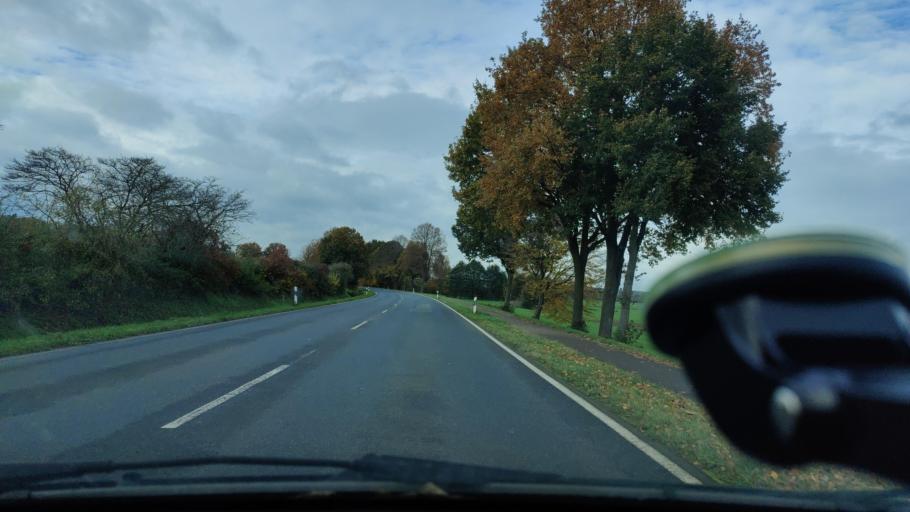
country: DE
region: North Rhine-Westphalia
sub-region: Regierungsbezirk Dusseldorf
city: Sonsbeck
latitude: 51.6354
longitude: 6.4023
